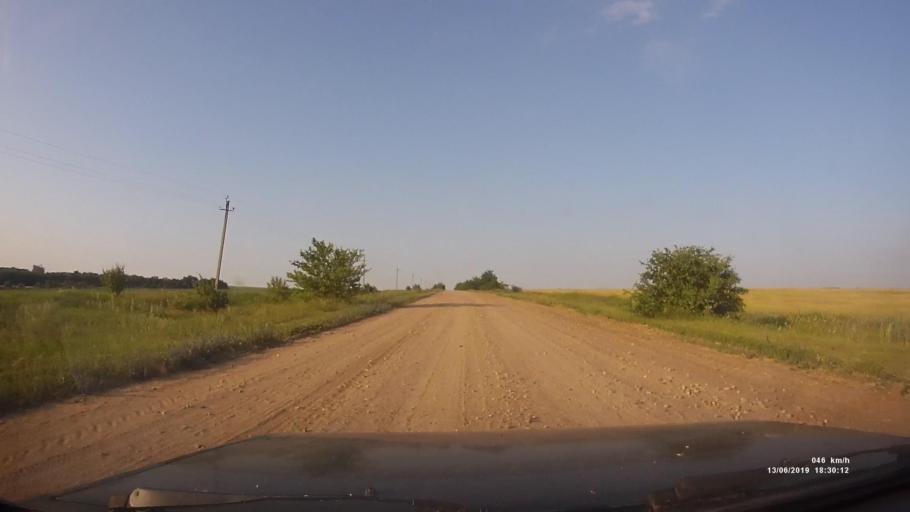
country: RU
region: Rostov
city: Kazanskaya
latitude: 49.8611
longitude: 41.3479
